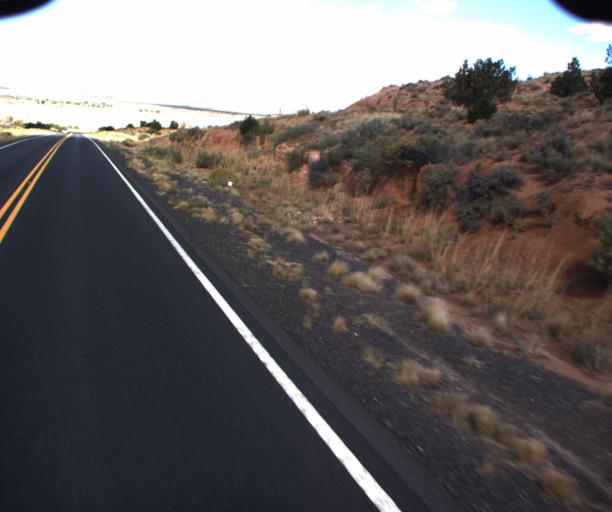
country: US
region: Arizona
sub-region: Apache County
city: Houck
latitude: 35.0341
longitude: -109.2609
